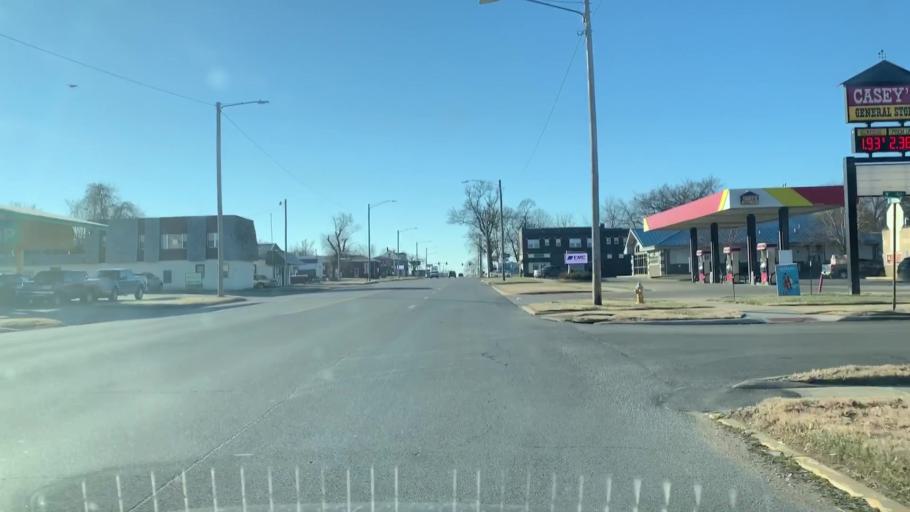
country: US
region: Kansas
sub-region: Crawford County
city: Pittsburg
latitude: 37.4034
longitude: -94.7050
